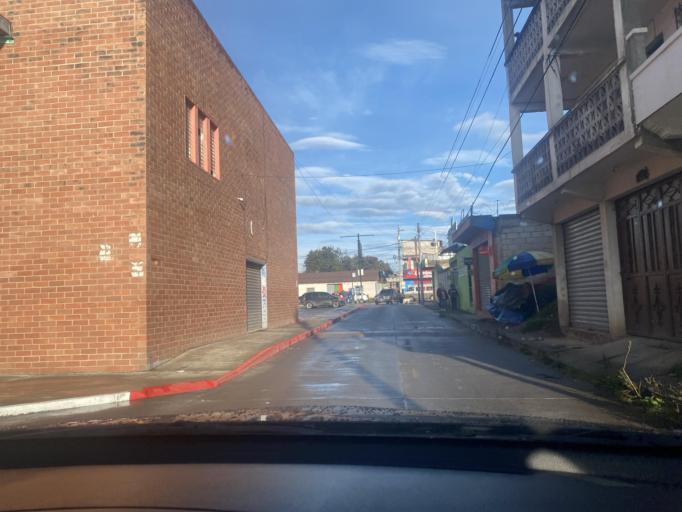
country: GT
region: Quetzaltenango
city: Olintepeque
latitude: 14.8624
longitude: -91.5212
